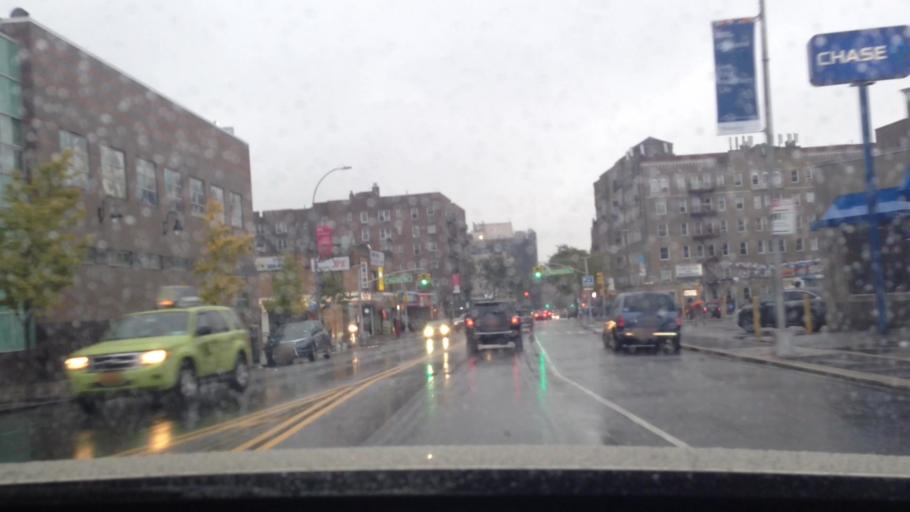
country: US
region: New York
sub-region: Queens County
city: Long Island City
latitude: 40.7444
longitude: -73.8859
